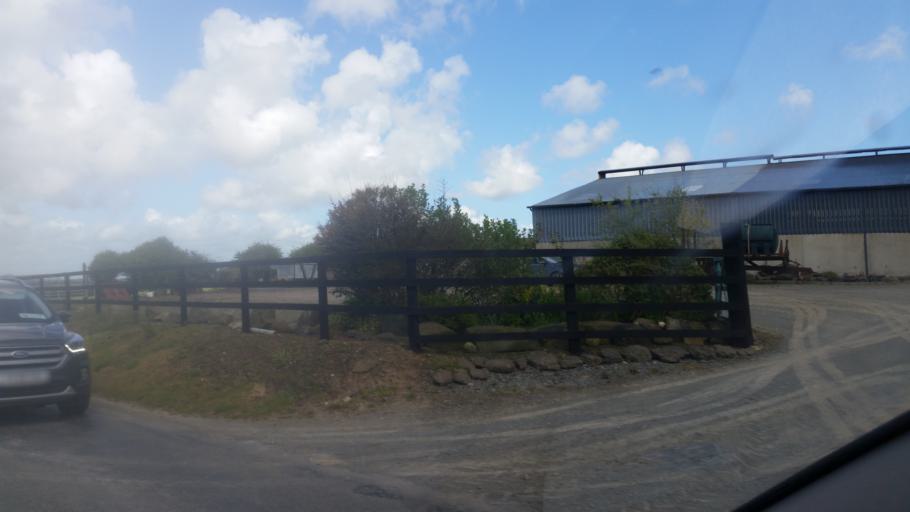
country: IE
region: Munster
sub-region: Waterford
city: Dunmore East
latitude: 52.1936
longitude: -6.8994
